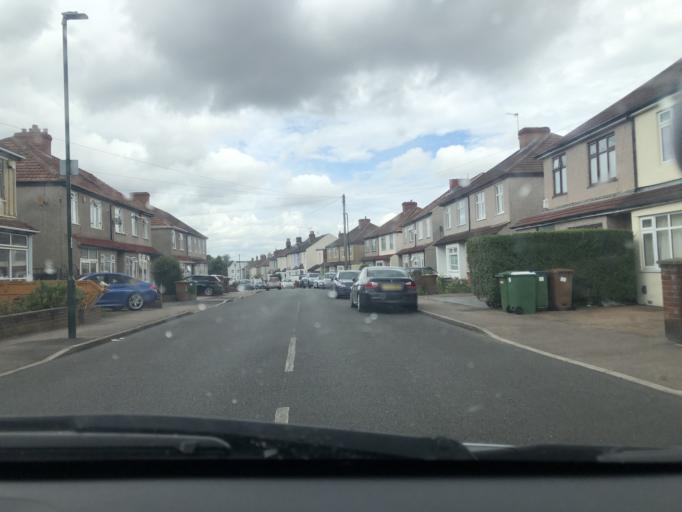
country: GB
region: England
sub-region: Greater London
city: Bexleyheath
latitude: 51.4564
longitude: 0.1271
